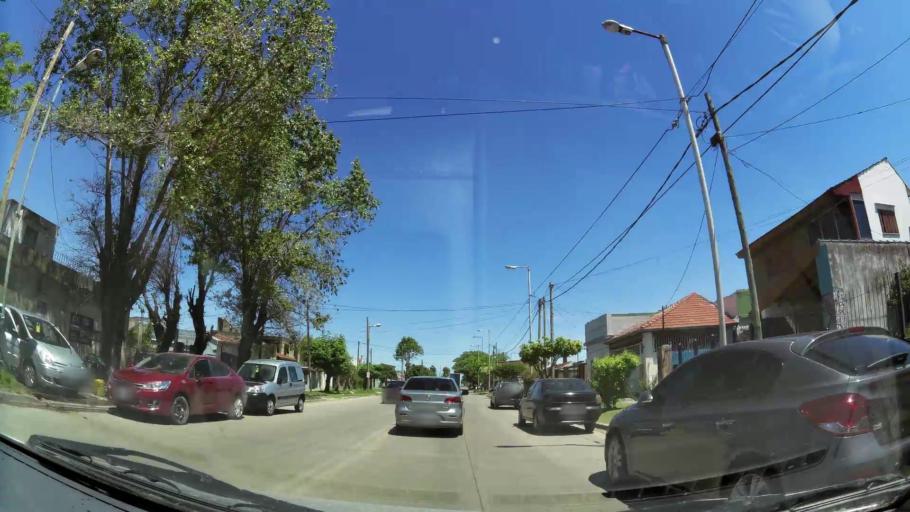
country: AR
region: Buenos Aires
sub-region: Partido de Quilmes
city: Quilmes
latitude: -34.7175
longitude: -58.3233
